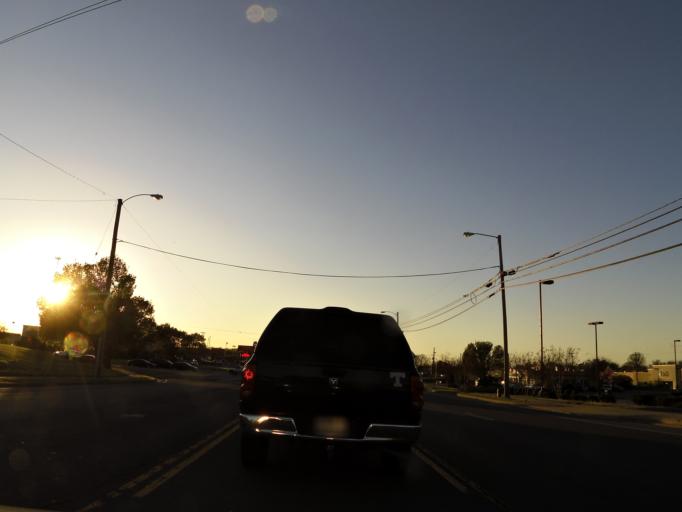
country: US
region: Tennessee
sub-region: Robertson County
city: Springfield
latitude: 36.4927
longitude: -86.8750
